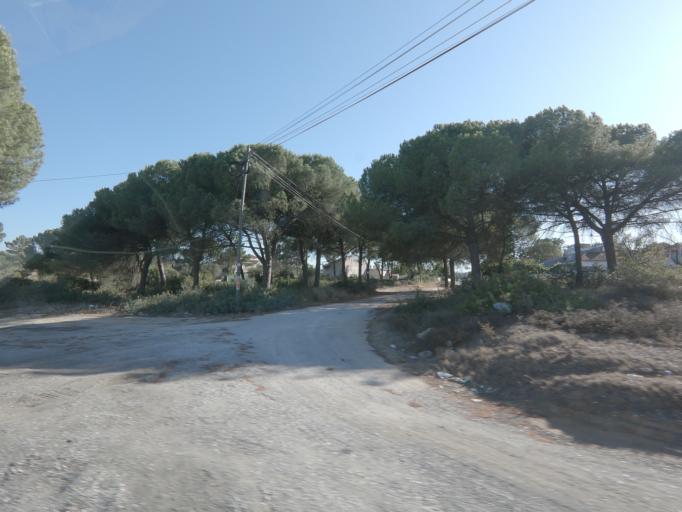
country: PT
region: Setubal
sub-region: Moita
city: Moita
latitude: 38.6256
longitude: -8.9602
